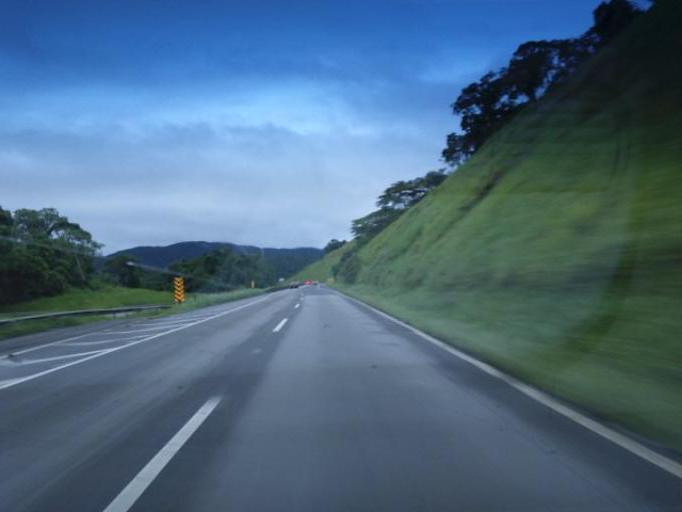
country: BR
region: Sao Paulo
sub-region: Miracatu
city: Miracatu
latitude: -24.1646
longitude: -47.3317
